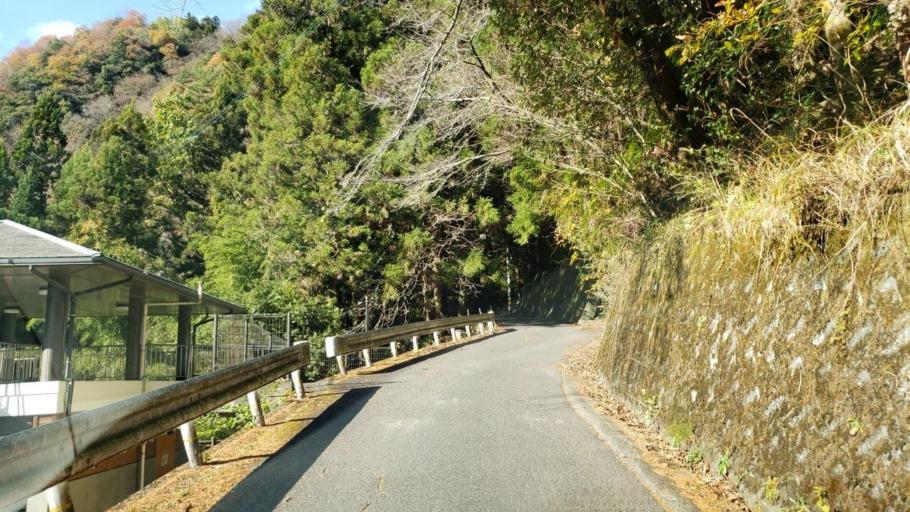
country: JP
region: Tokushima
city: Wakimachi
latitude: 33.9902
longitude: 134.0025
